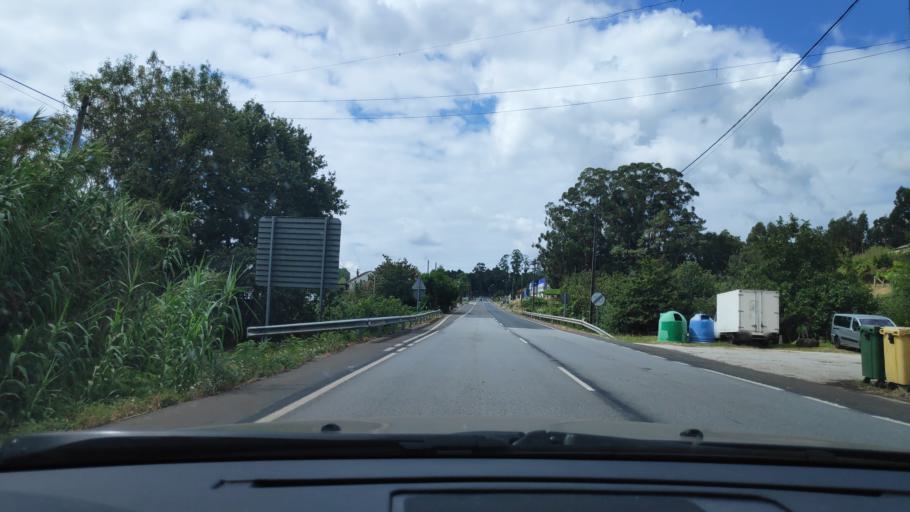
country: ES
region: Galicia
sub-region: Provincia de Pontevedra
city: Portas
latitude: 42.5845
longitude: -8.6952
